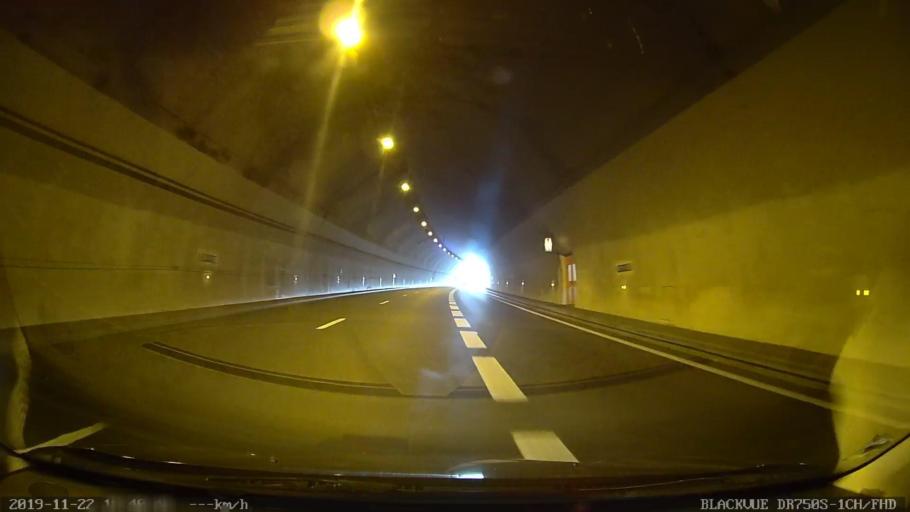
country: RE
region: Reunion
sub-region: Reunion
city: Saint-Paul
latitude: -21.0293
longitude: 55.2542
